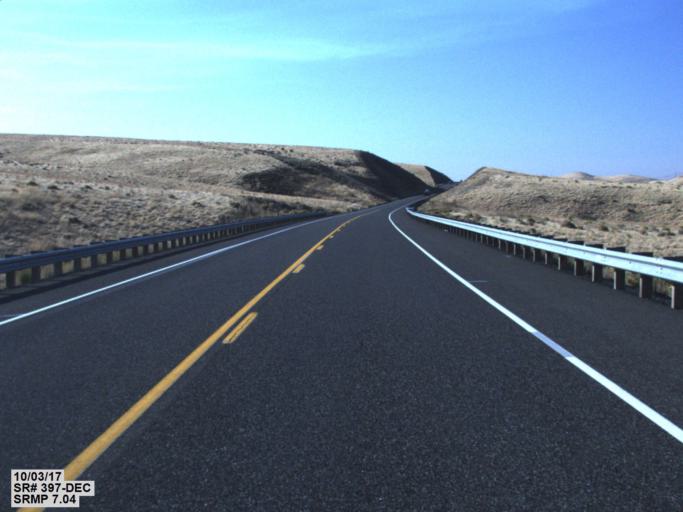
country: US
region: Washington
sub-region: Benton County
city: Highland
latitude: 46.1277
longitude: -119.0706
